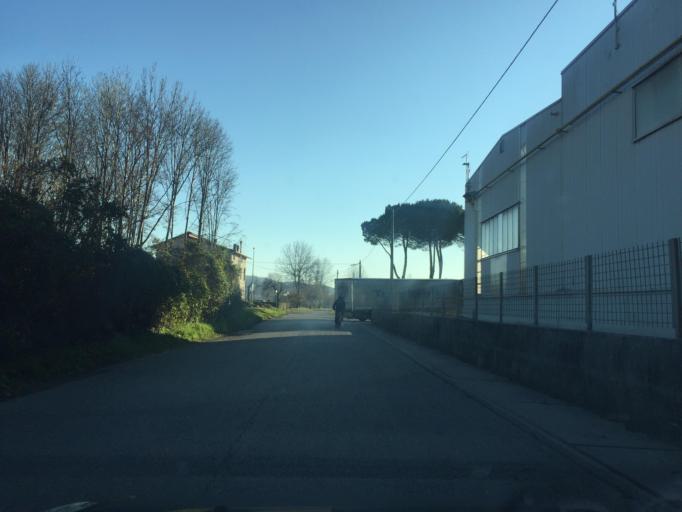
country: IT
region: Friuli Venezia Giulia
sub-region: Provincia di Udine
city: Osoppo
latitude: 46.2500
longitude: 13.1097
